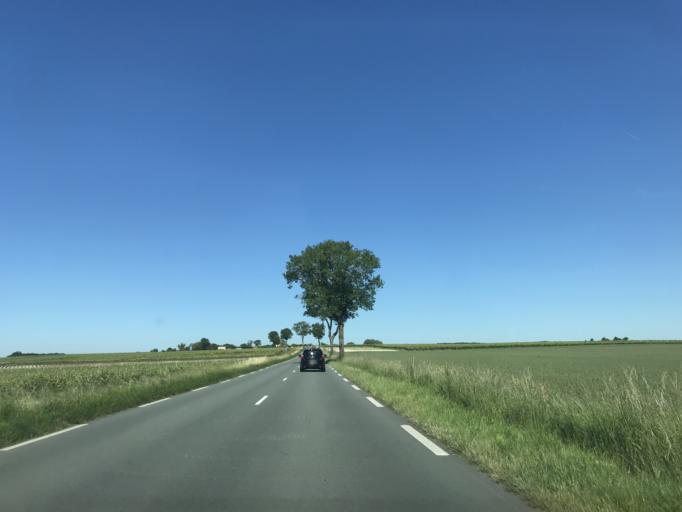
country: FR
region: Poitou-Charentes
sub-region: Departement de la Charente-Maritime
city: Perignac
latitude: 45.5762
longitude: -0.4327
